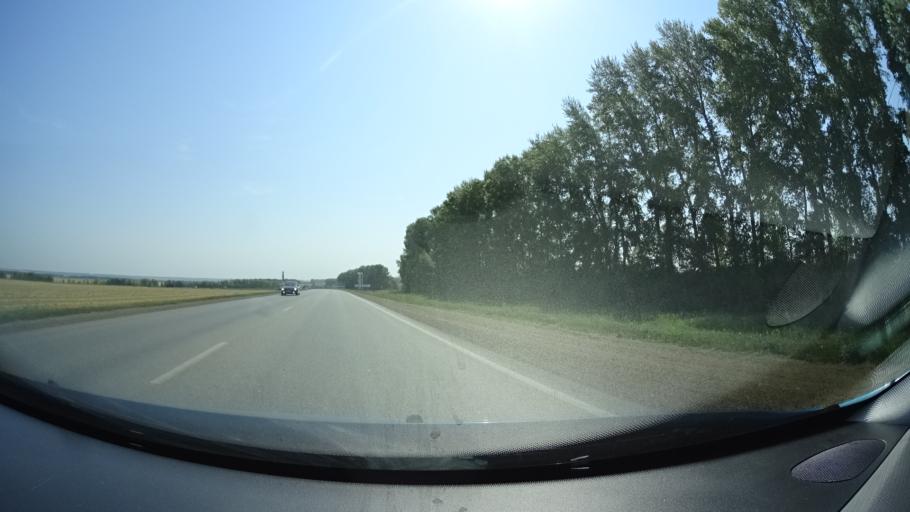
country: RU
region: Bashkortostan
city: Kabakovo
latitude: 54.4709
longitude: 55.9448
